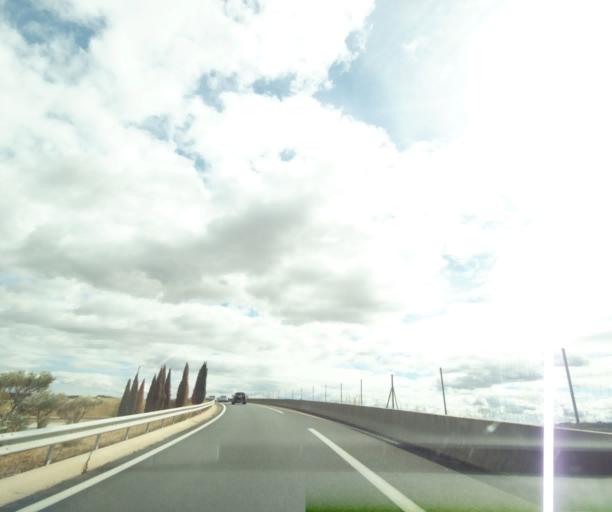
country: FR
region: Languedoc-Roussillon
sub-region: Departement de l'Herault
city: Nebian
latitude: 43.6559
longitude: 3.4460
